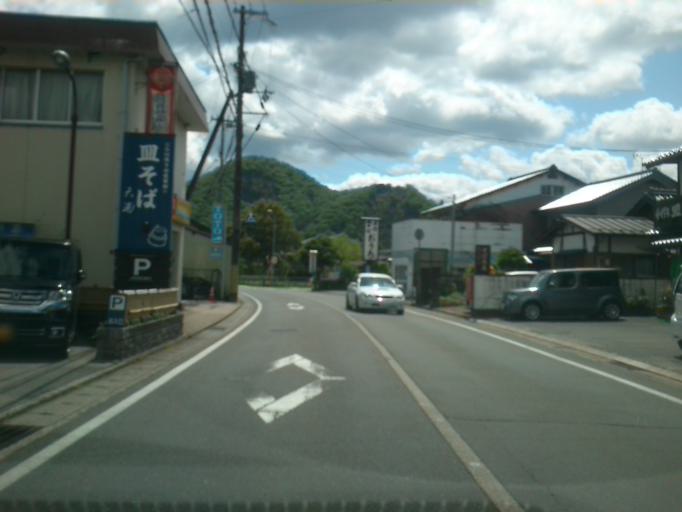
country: JP
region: Hyogo
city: Toyooka
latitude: 35.4601
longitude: 134.8712
